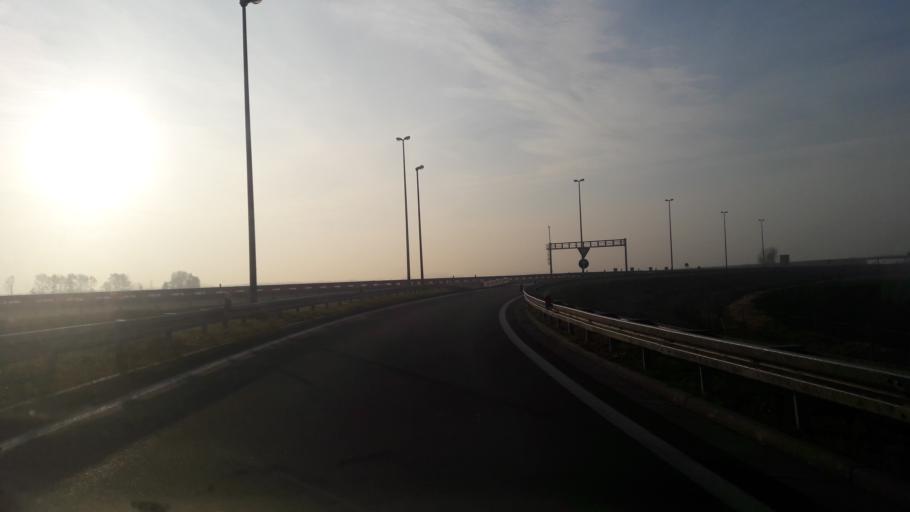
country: HR
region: Osjecko-Baranjska
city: Josipovac
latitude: 45.5733
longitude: 18.5504
